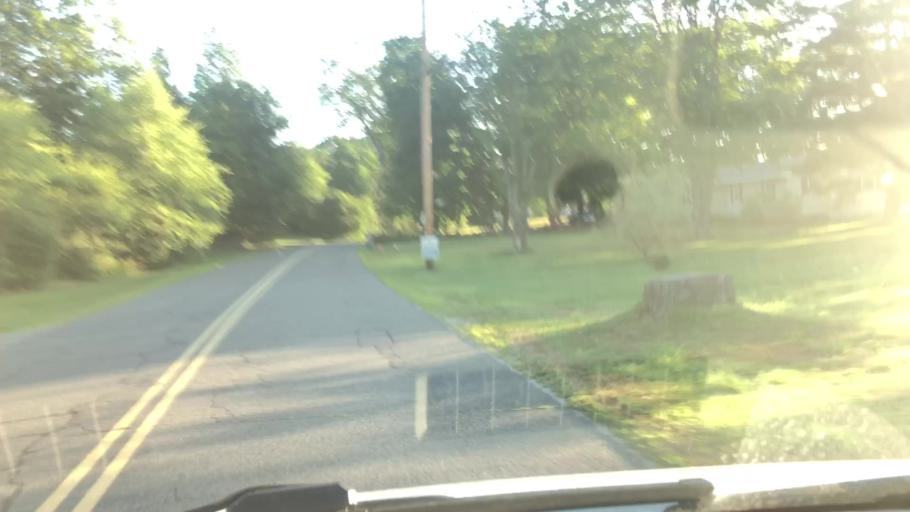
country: US
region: Massachusetts
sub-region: Hampshire County
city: Williamsburg
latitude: 42.3735
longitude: -72.7318
